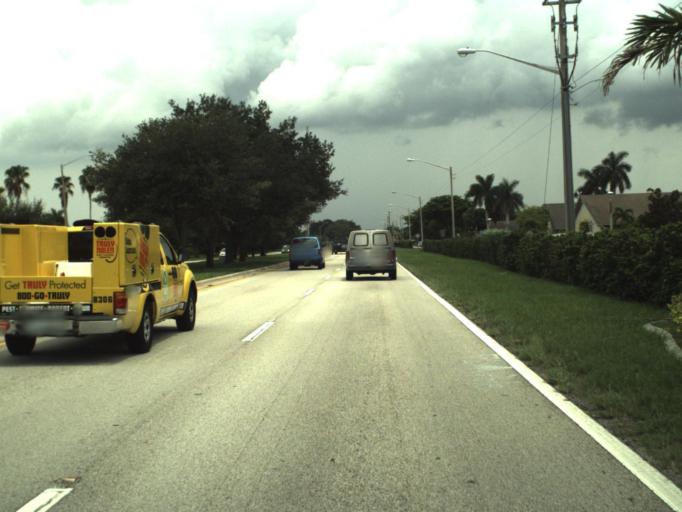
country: US
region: Florida
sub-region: Broward County
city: Cooper City
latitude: 26.0298
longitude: -80.2854
